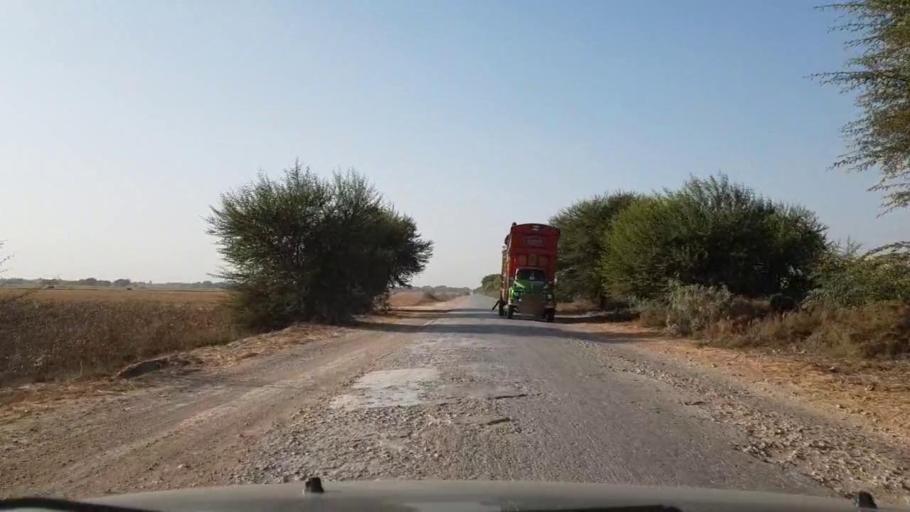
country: PK
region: Sindh
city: Chambar
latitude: 25.1999
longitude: 68.7960
